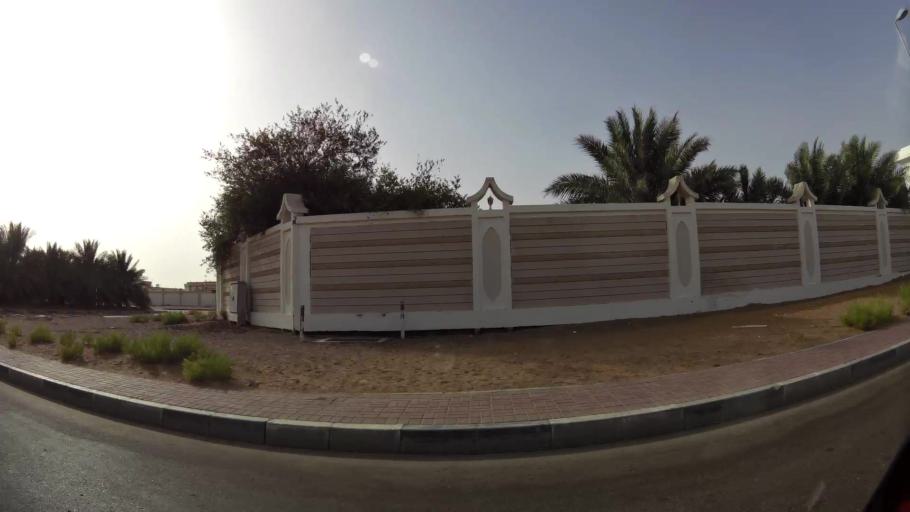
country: AE
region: Abu Dhabi
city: Al Ain
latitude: 24.2178
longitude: 55.6470
